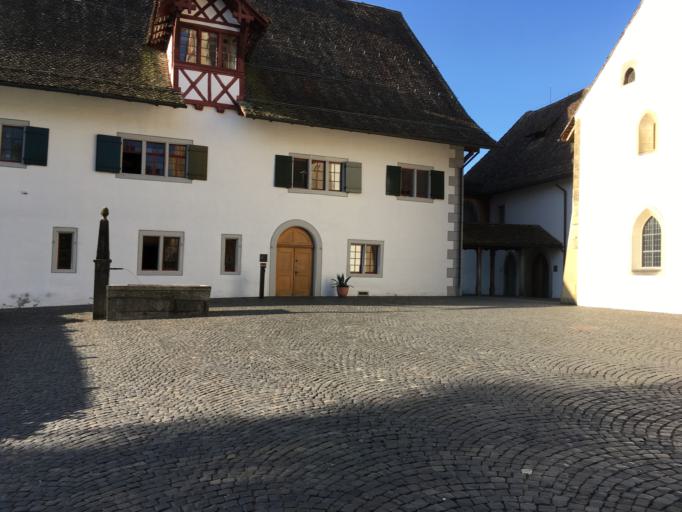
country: CH
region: Zurich
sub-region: Bezirk Affoltern
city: Hausen am Albis / Hausen (Dorf)
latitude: 47.2273
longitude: 8.5250
